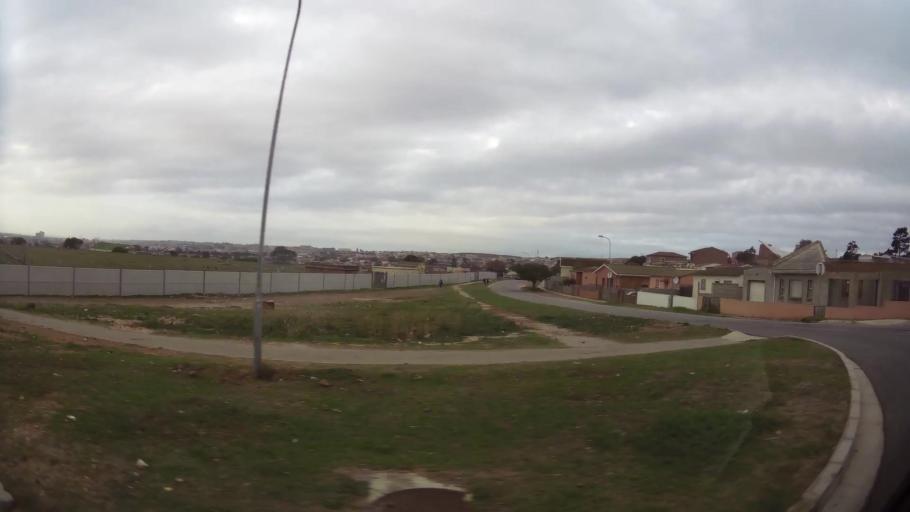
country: ZA
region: Eastern Cape
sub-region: Nelson Mandela Bay Metropolitan Municipality
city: Port Elizabeth
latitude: -33.9113
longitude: 25.5504
